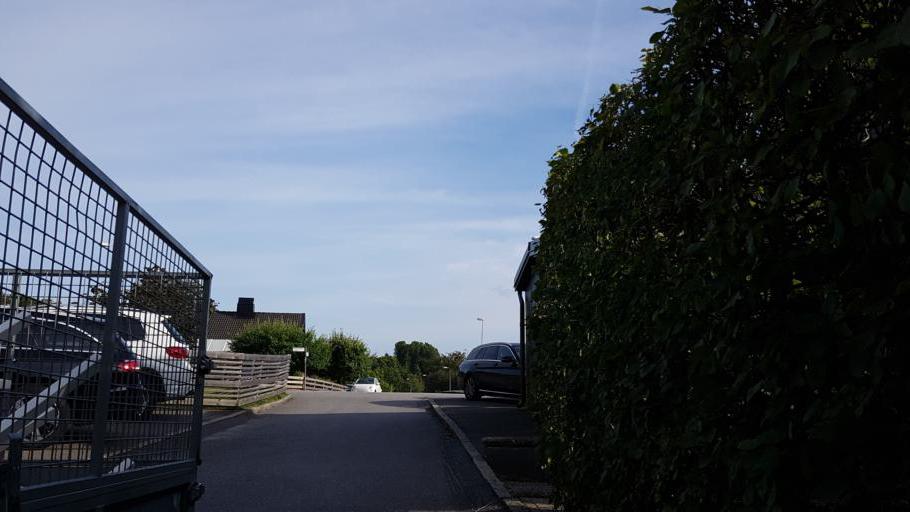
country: SE
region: Vaestra Goetaland
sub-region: Molndal
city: Moelndal
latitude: 57.6684
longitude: 12.0325
